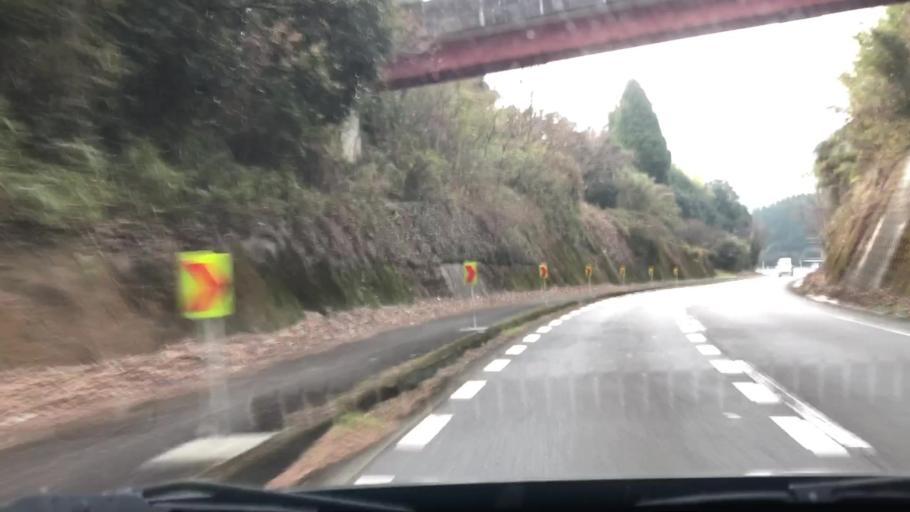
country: JP
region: Oita
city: Takedamachi
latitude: 32.9773
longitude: 131.5592
